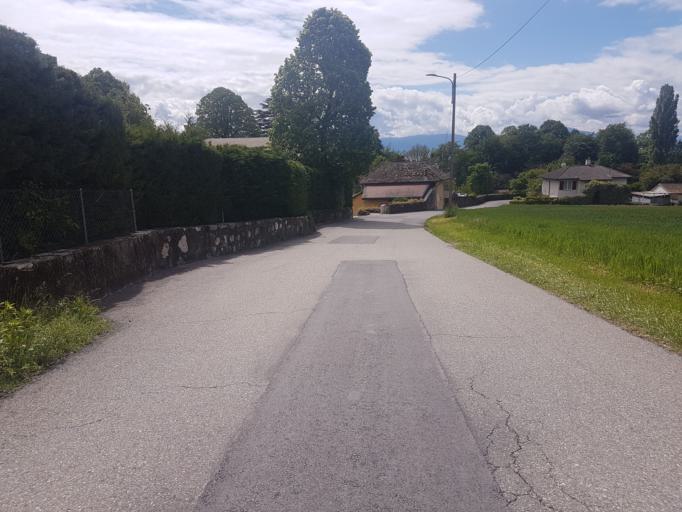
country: CH
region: Vaud
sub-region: Nyon District
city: Rolle
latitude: 46.4658
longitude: 6.3380
